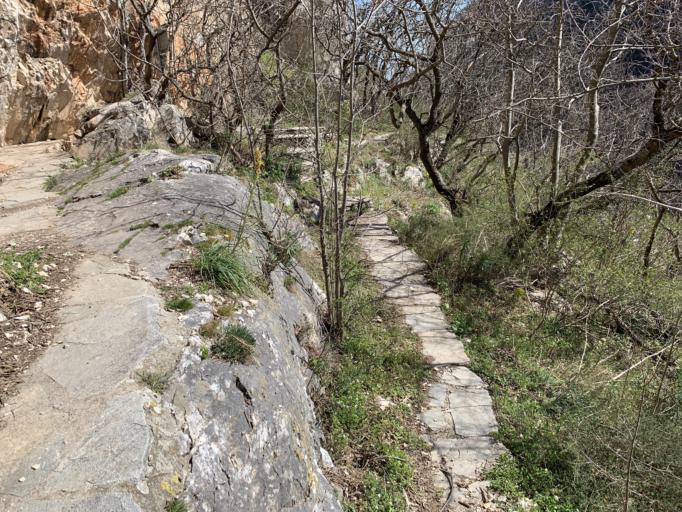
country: GR
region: Central Macedonia
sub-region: Nomos Pellis
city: Loutraki
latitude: 40.9726
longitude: 21.9083
